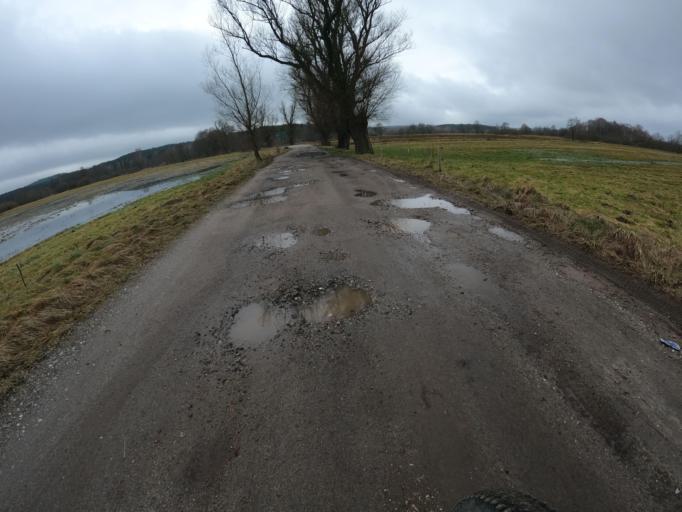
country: PL
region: West Pomeranian Voivodeship
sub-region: Powiat slawienski
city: Slawno
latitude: 54.2550
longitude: 16.6454
